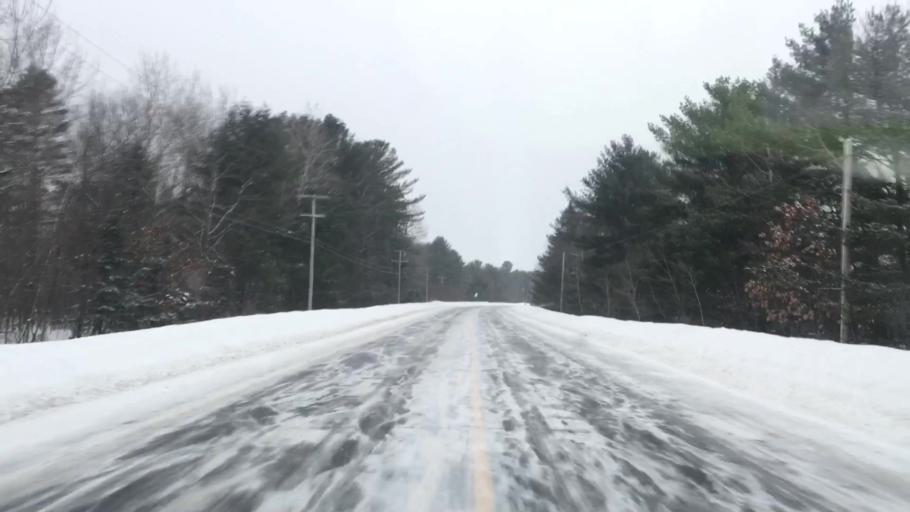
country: US
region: Maine
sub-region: Penobscot County
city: Medway
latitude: 45.5635
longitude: -68.3966
